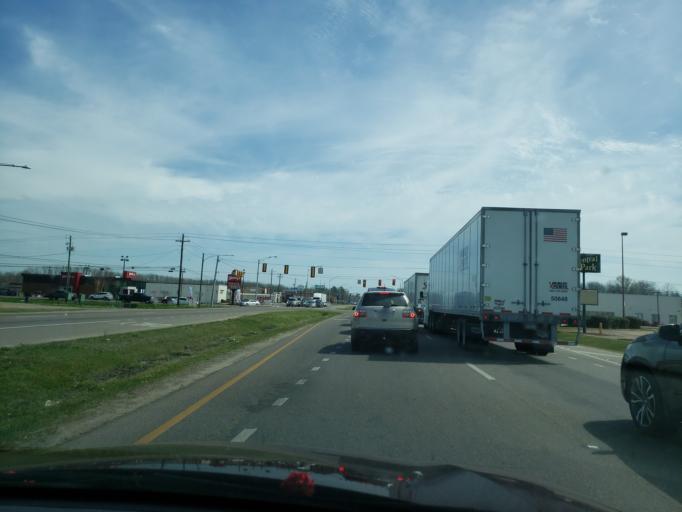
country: US
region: Alabama
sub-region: Dallas County
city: Selma
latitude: 32.4313
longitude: -87.0154
